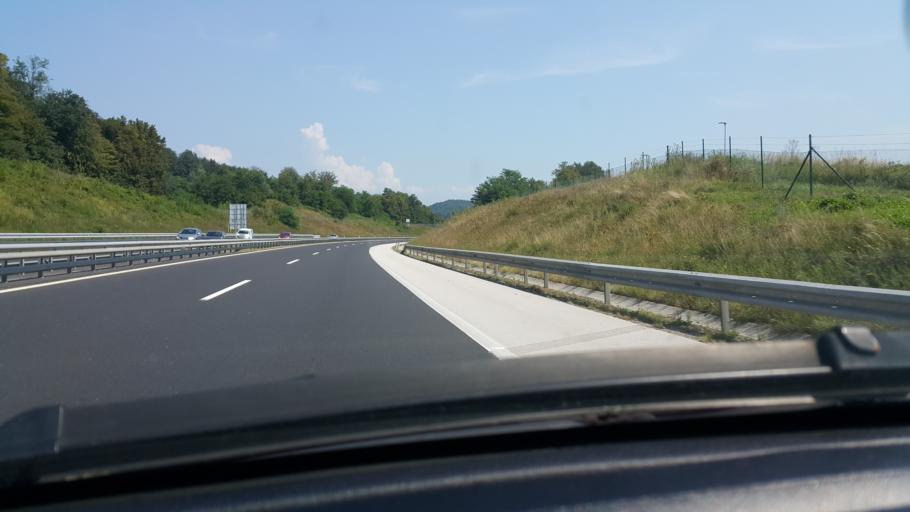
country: SI
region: Novo Mesto
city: Novo Mesto
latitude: 45.8307
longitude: 15.2004
